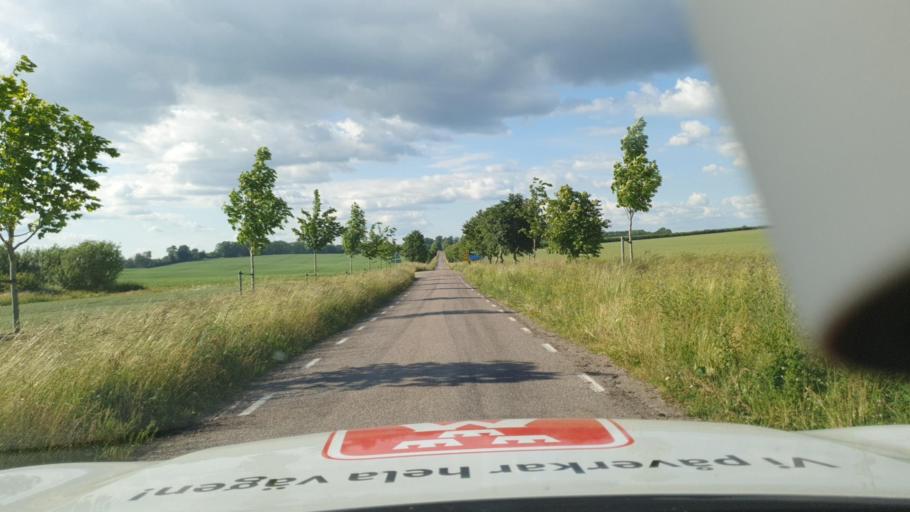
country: SE
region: Skane
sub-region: Ystads Kommun
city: Ystad
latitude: 55.4343
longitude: 13.7373
